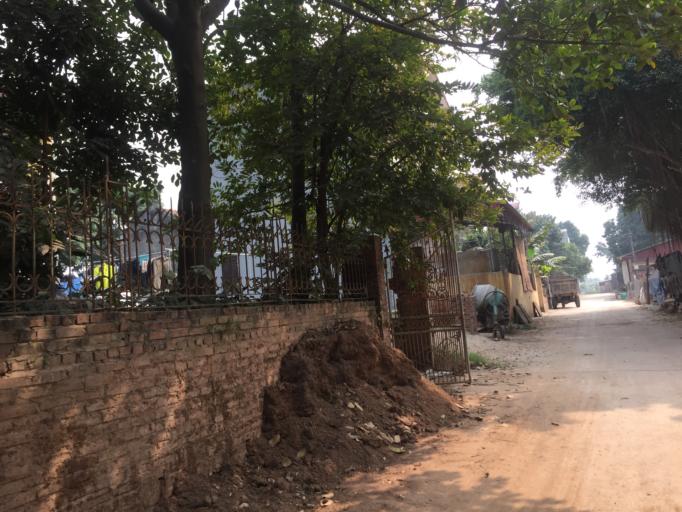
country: VN
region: Hung Yen
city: Van Giang
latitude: 20.9461
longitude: 105.9097
